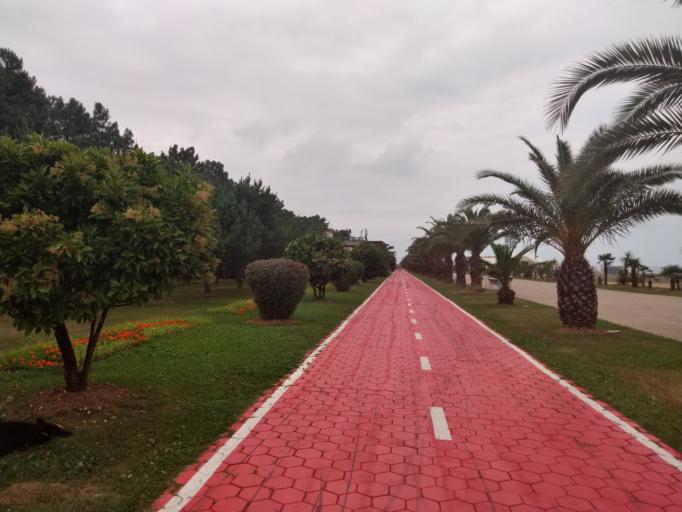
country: GE
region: Ajaria
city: Batumi
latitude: 41.6548
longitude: 41.6328
